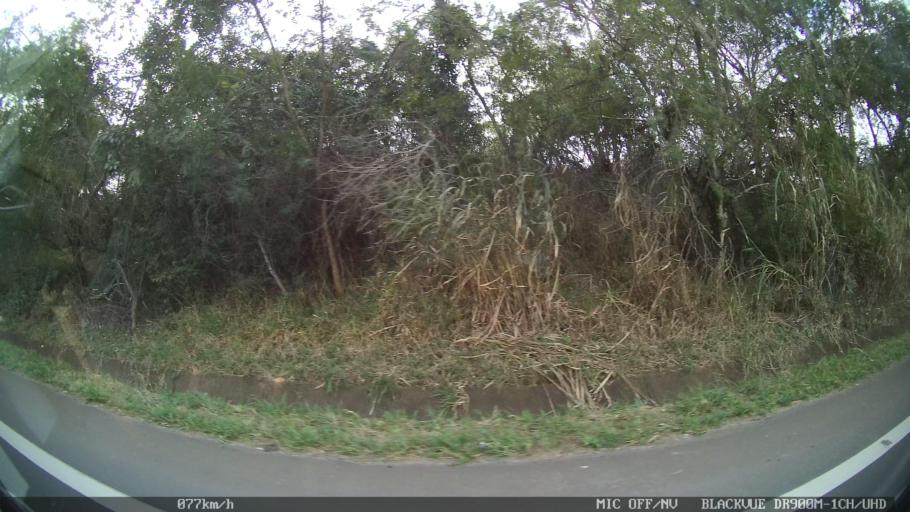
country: BR
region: Sao Paulo
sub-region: Cosmopolis
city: Cosmopolis
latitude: -22.6323
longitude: -47.3015
